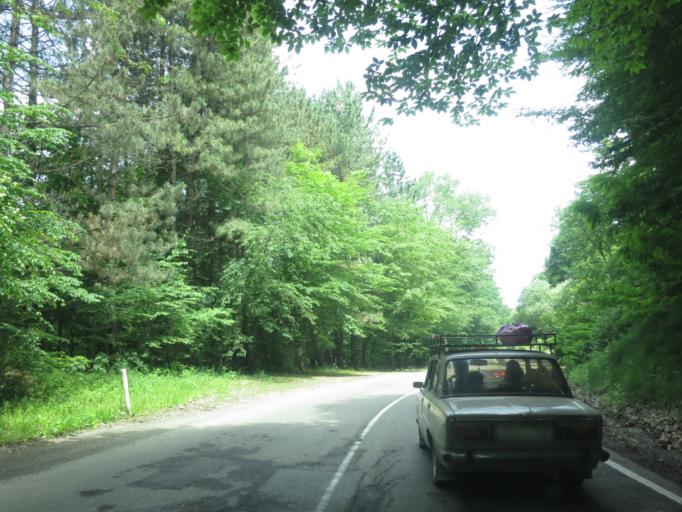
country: GE
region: Kakheti
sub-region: Telavi
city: Telavi
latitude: 41.8770
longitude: 45.3555
